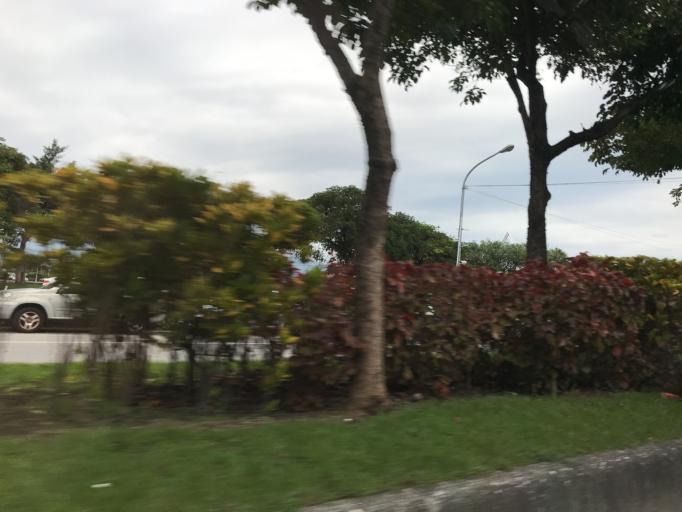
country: TW
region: Taiwan
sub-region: Yilan
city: Yilan
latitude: 24.7096
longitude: 121.7725
